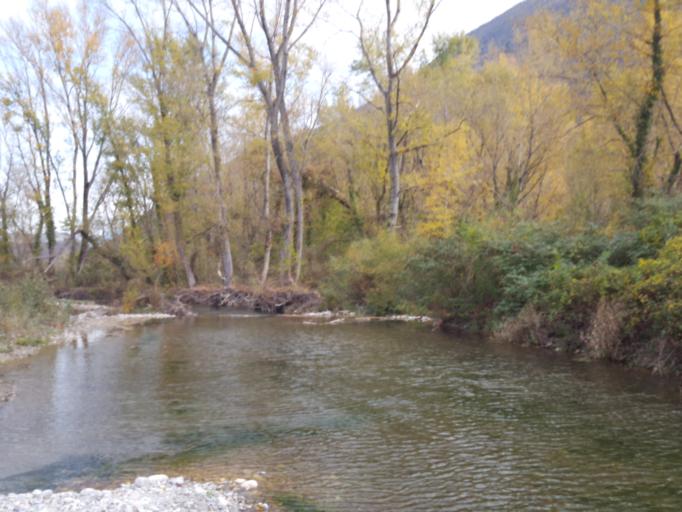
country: FR
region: Rhone-Alpes
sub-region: Departement de l'Isere
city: Saint-Georges-de-Commiers
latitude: 45.0526
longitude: 5.7077
